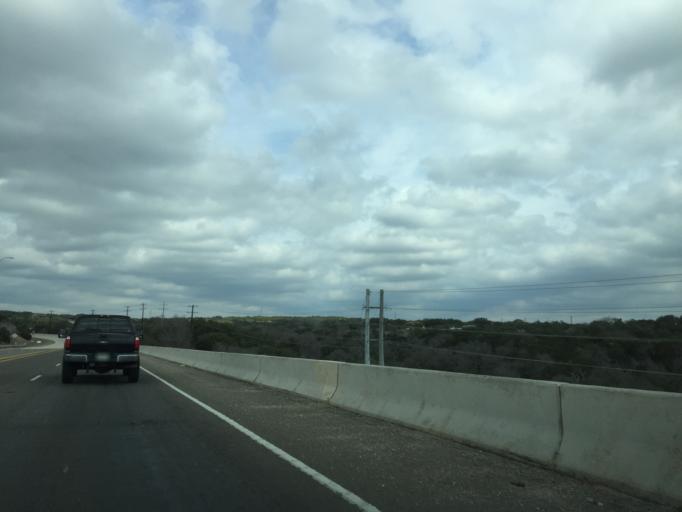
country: US
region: Texas
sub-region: Travis County
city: Briarcliff
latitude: 30.3897
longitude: -98.0863
